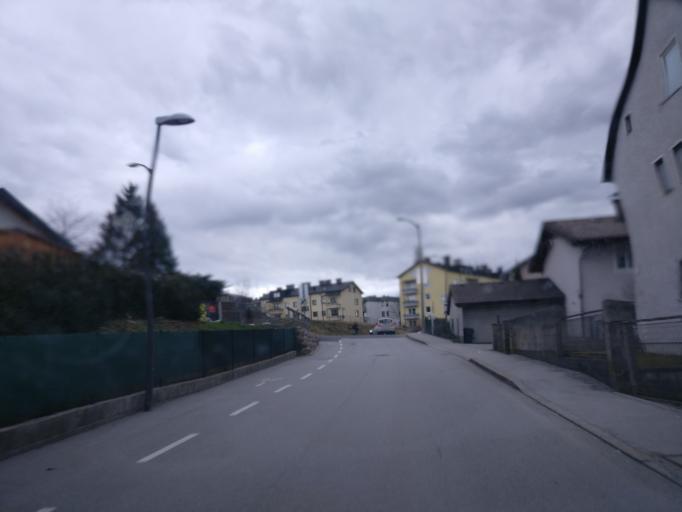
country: AT
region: Salzburg
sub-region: Politischer Bezirk Salzburg-Umgebung
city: Bergheim
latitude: 47.8242
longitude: 13.0402
